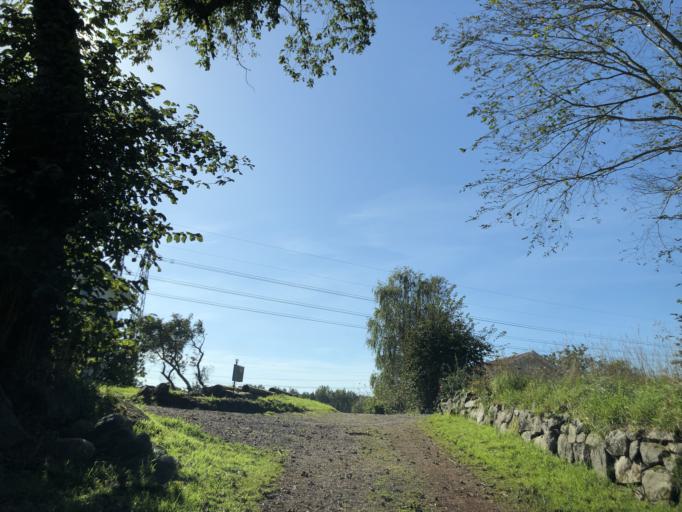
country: SE
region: Vaestra Goetaland
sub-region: Goteborg
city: Goeteborg
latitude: 57.7700
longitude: 11.9286
